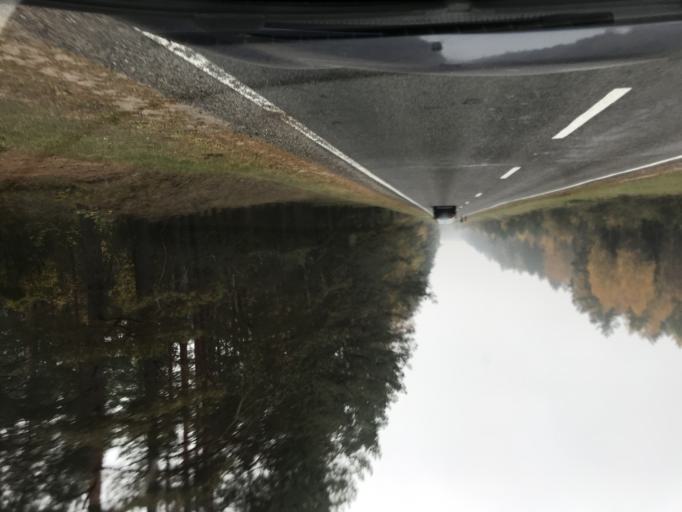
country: LT
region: Alytaus apskritis
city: Druskininkai
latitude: 53.8801
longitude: 23.9027
